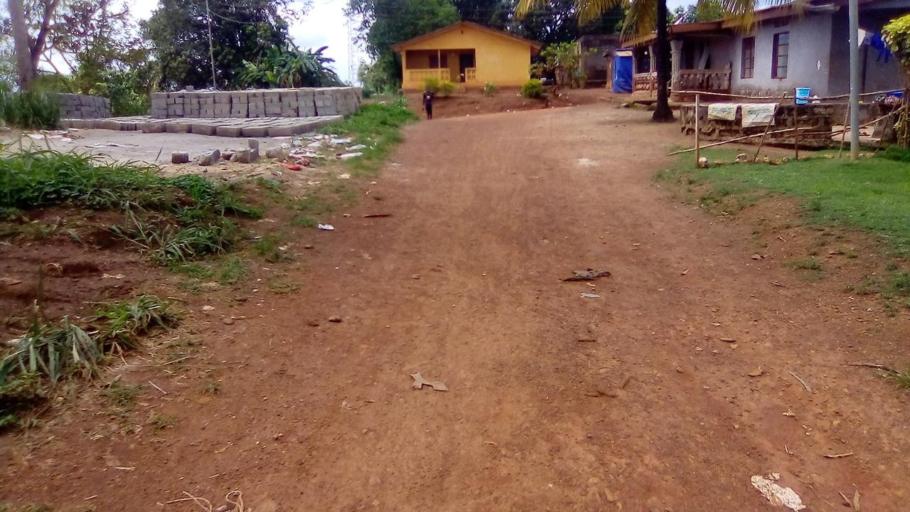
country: SL
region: Southern Province
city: Bo
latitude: 7.9684
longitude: -11.7182
